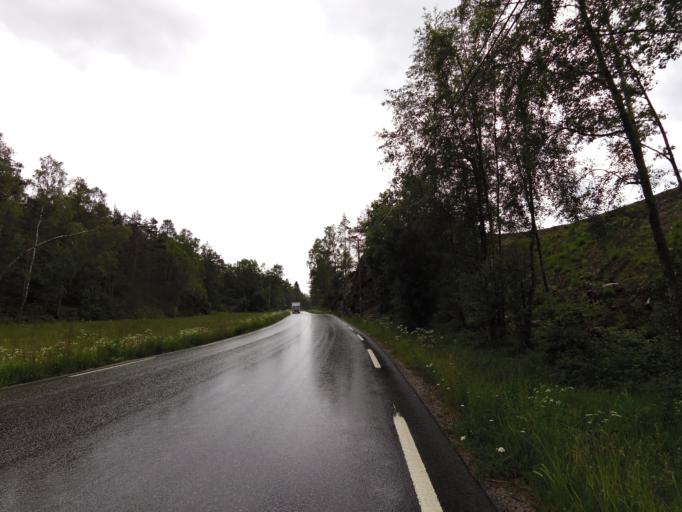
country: NO
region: Vest-Agder
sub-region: Mandal
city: Mandal
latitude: 58.0218
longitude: 7.5163
